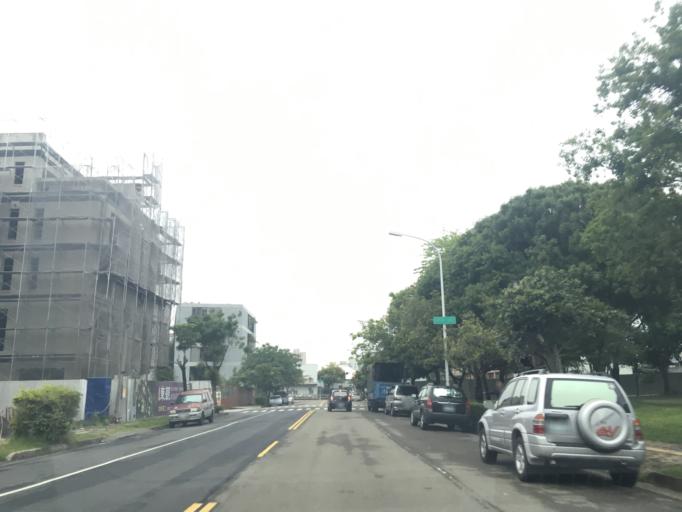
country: TW
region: Taiwan
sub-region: Taichung City
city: Taichung
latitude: 24.1674
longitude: 120.7120
